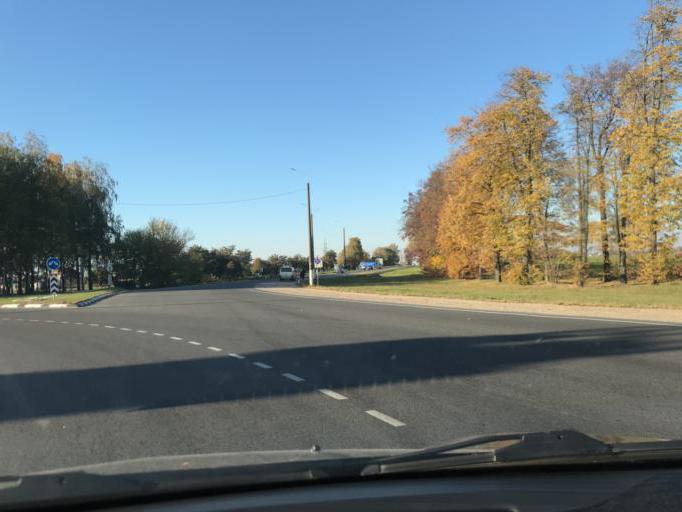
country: BY
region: Minsk
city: Slutsk
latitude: 53.0524
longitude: 27.5546
